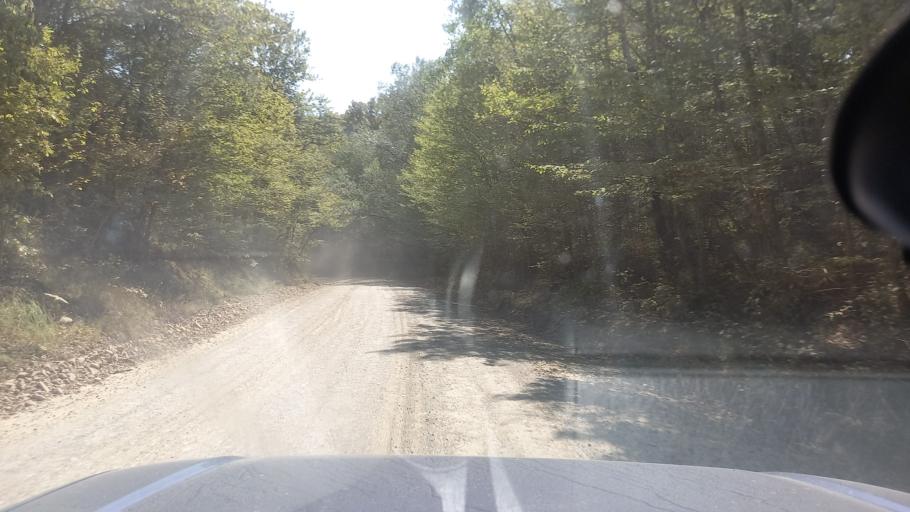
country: RU
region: Krasnodarskiy
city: Azovskaya
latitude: 44.6777
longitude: 38.6336
